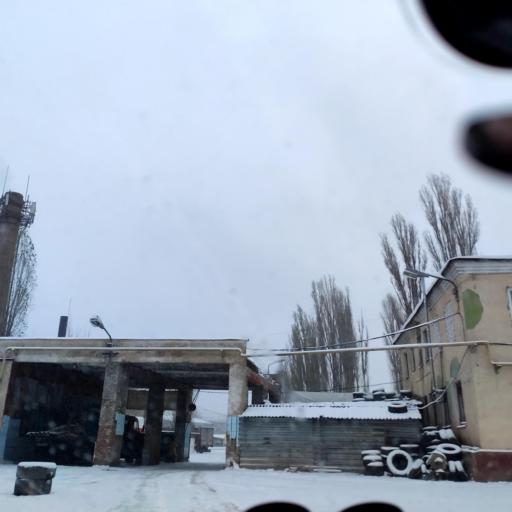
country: RU
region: Voronezj
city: Voronezh
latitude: 51.6633
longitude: 39.1466
